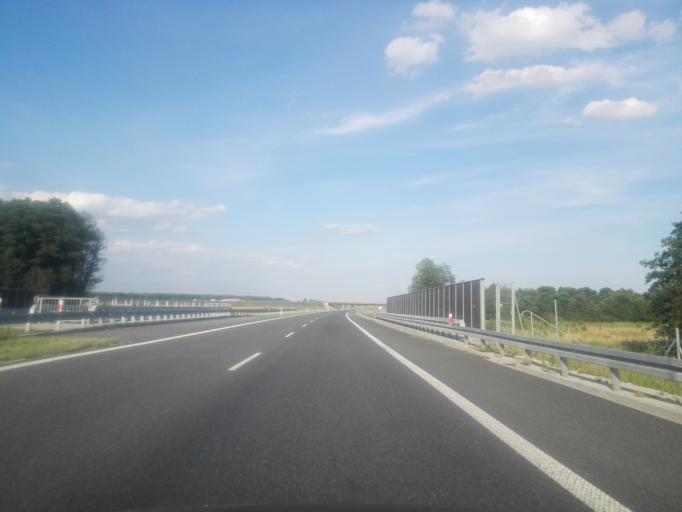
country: PL
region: Greater Poland Voivodeship
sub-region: Powiat kepinski
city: Kepno
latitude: 51.3164
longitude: 17.9703
